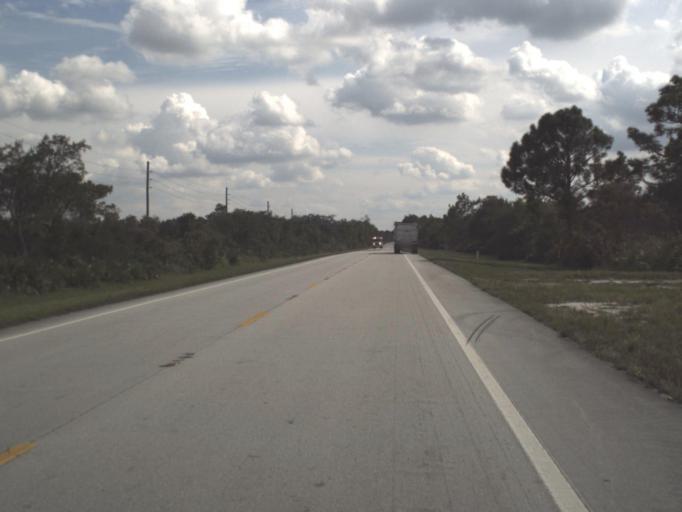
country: US
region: Florida
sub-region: Okeechobee County
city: Cypress Quarters
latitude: 27.5417
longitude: -80.8132
